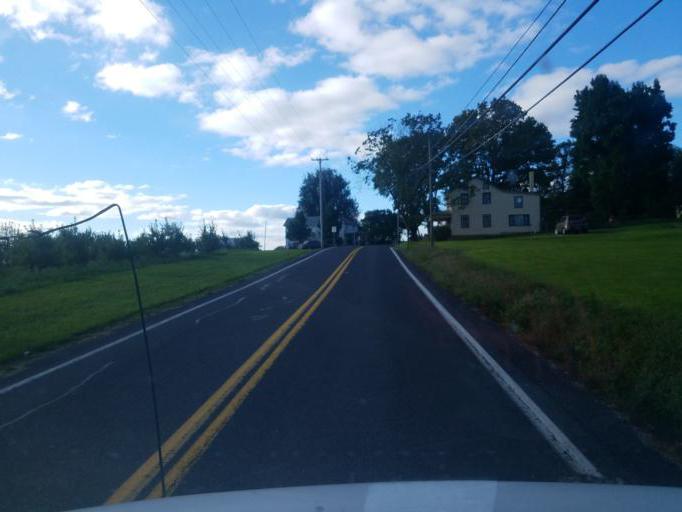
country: US
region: Pennsylvania
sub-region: Adams County
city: Biglerville
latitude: 39.8895
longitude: -77.3568
